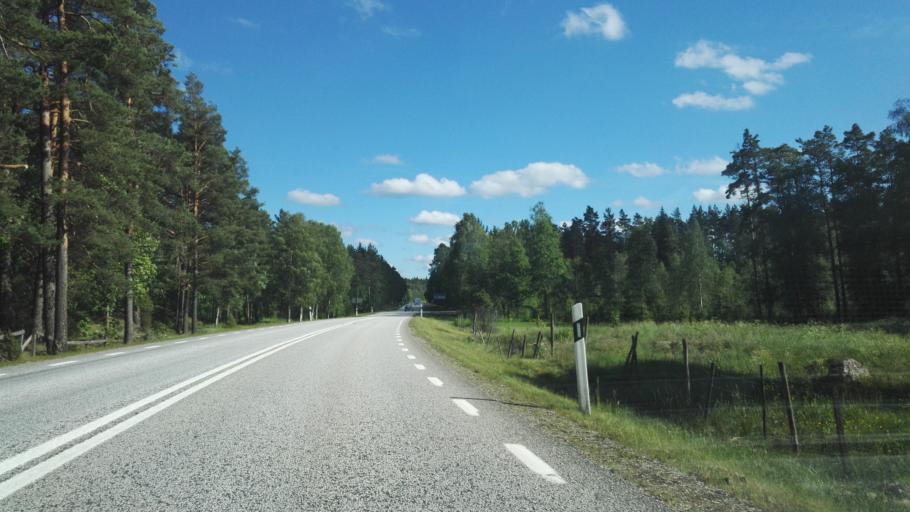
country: SE
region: Joenkoeping
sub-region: Savsjo Kommun
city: Vrigstad
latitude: 57.3076
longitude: 14.5153
